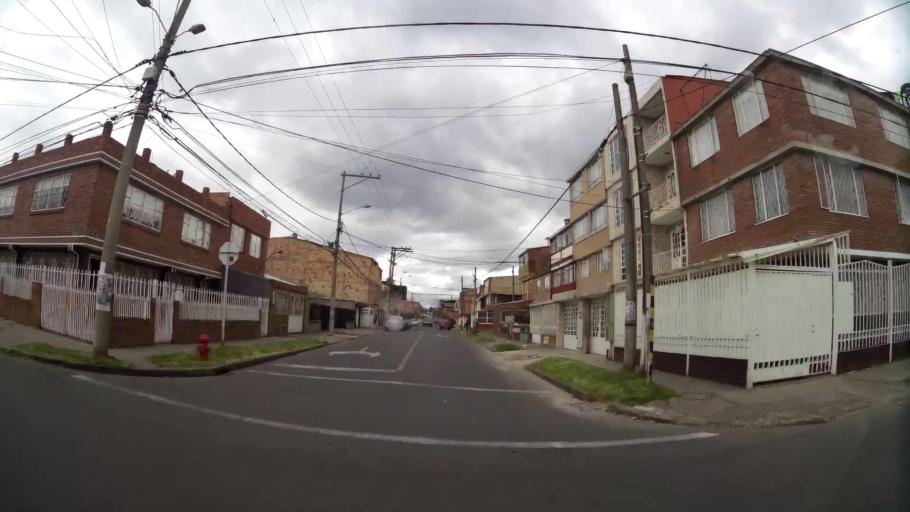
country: CO
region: Bogota D.C.
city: Bogota
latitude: 4.6086
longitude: -74.1344
